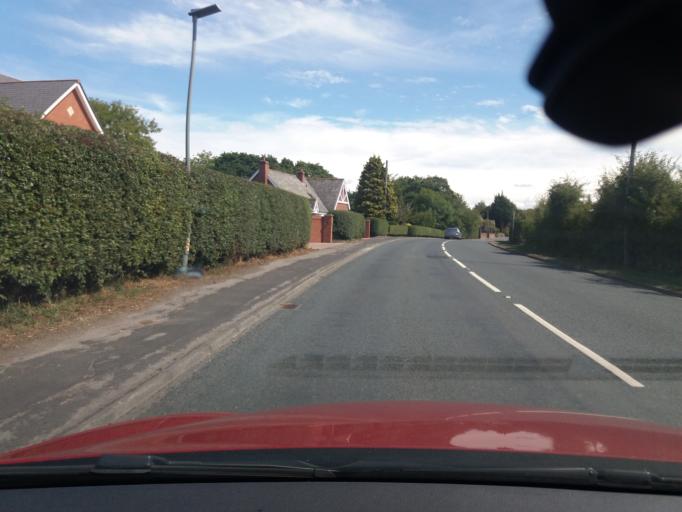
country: GB
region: England
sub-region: Lancashire
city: Euxton
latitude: 53.6602
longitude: -2.7008
